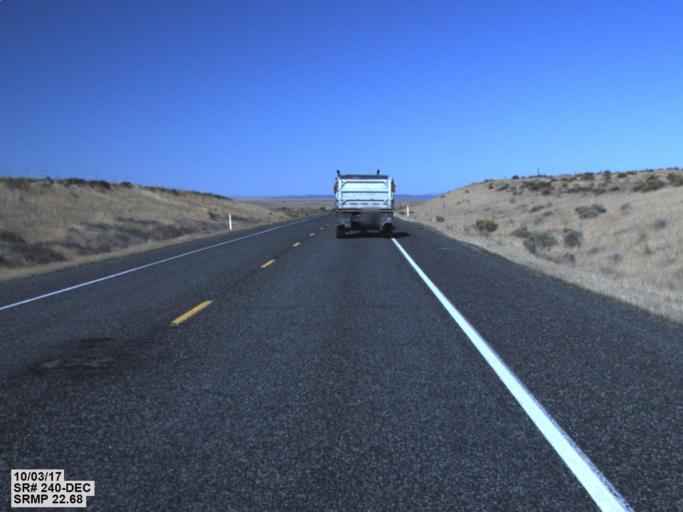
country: US
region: Washington
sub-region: Benton County
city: West Richland
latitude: 46.3635
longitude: -119.3866
